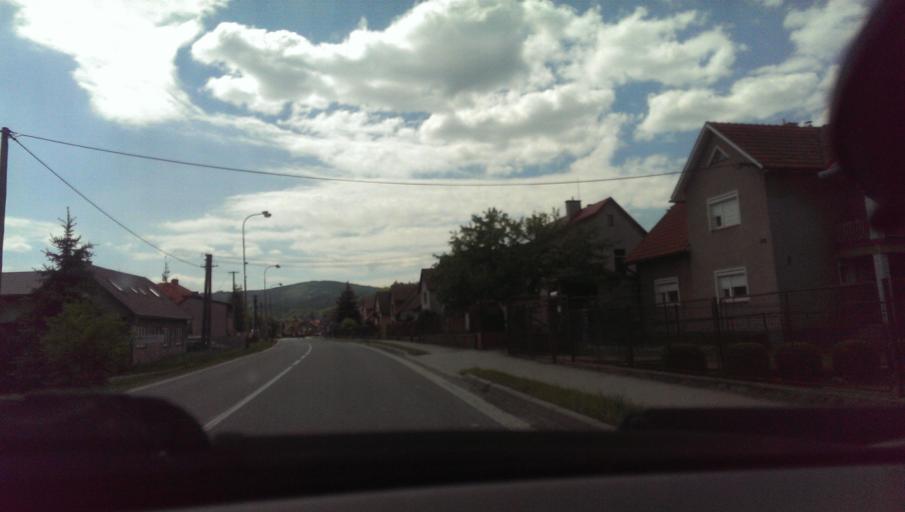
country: CZ
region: Zlin
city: Valasska Polanka
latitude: 49.2641
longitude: 17.9965
